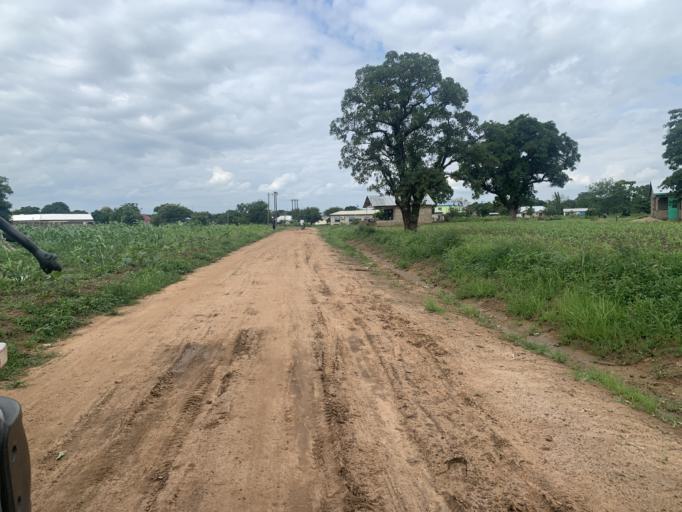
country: GH
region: Upper East
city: Navrongo
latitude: 10.8649
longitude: -1.0732
